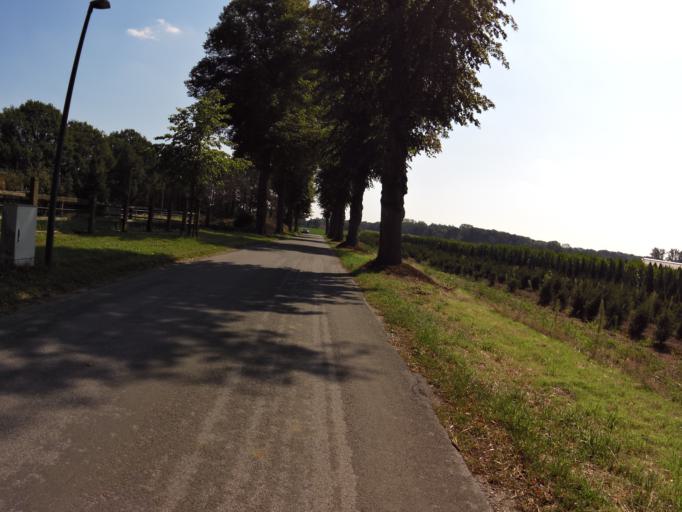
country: DE
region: North Rhine-Westphalia
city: Stadtlohn
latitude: 51.9995
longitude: 6.9472
